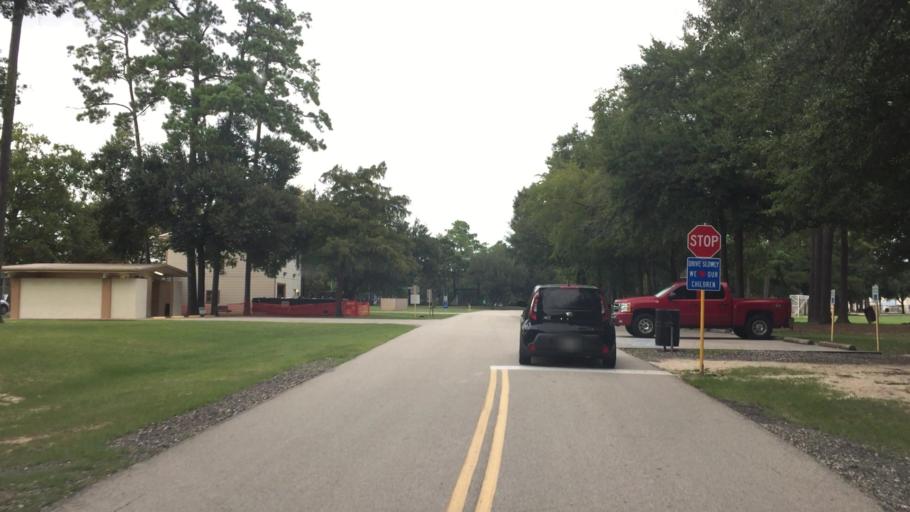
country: US
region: Texas
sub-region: Harris County
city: Hudson
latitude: 30.0104
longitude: -95.5085
